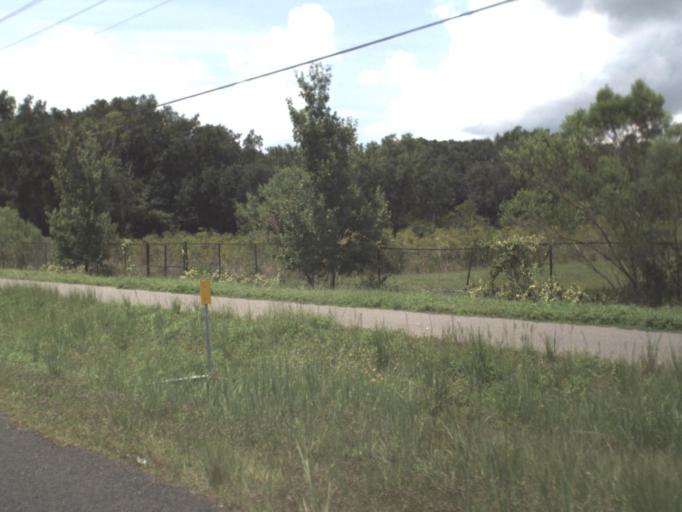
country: US
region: Florida
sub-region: Pasco County
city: Wesley Chapel
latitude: 28.2069
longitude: -82.3536
